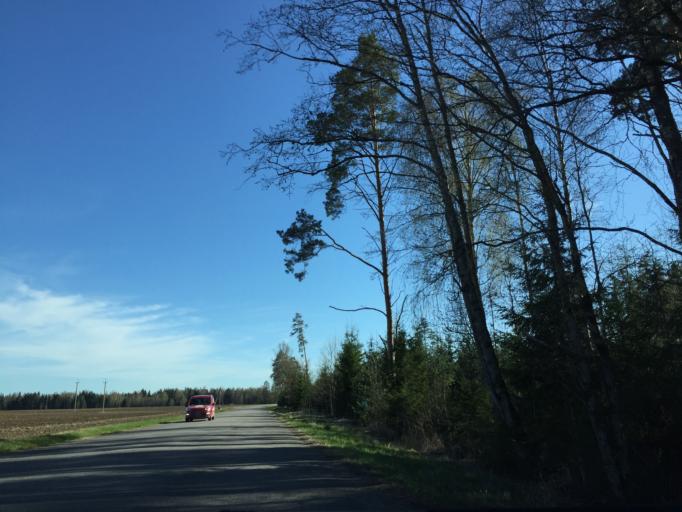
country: EE
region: Valgamaa
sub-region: Valga linn
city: Valga
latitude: 57.8579
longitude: 26.2532
